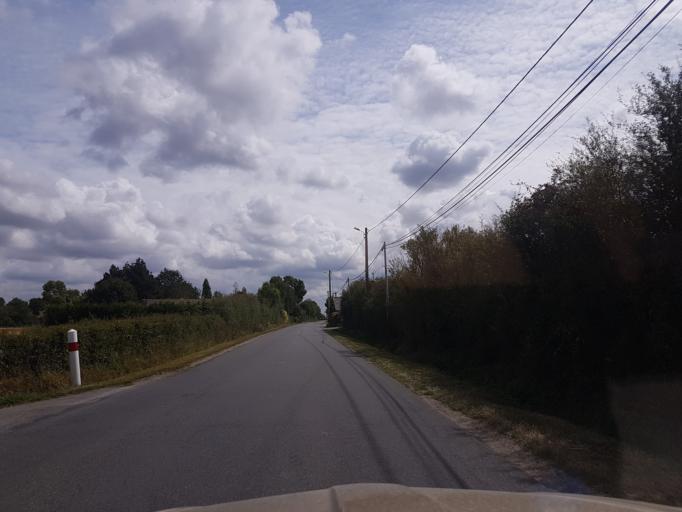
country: FR
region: Pays de la Loire
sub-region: Departement de la Loire-Atlantique
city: Les Touches
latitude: 47.4161
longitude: -1.4146
